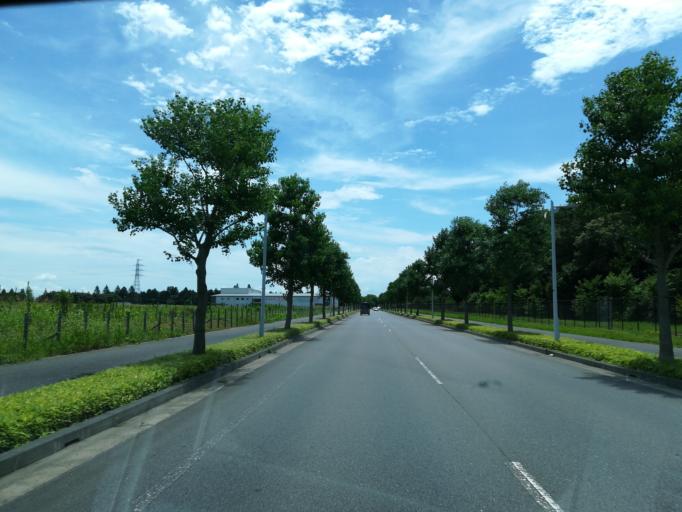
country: JP
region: Ibaraki
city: Naka
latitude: 36.0775
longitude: 140.0793
